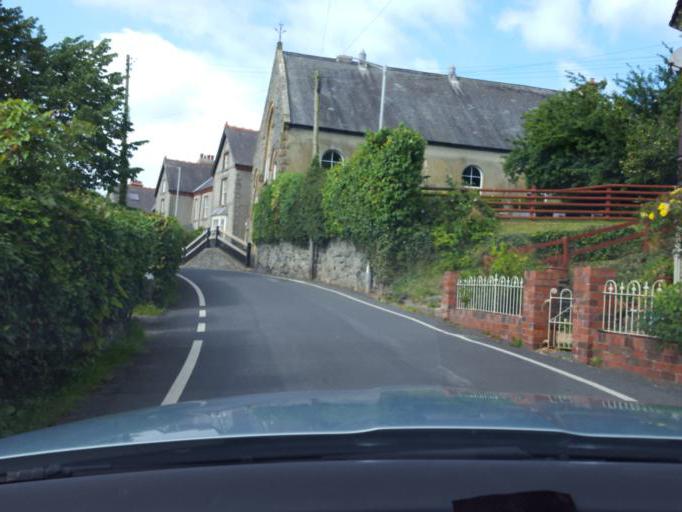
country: GB
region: Wales
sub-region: Denbighshire
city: Bryneglwys
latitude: 52.9837
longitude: -3.3200
